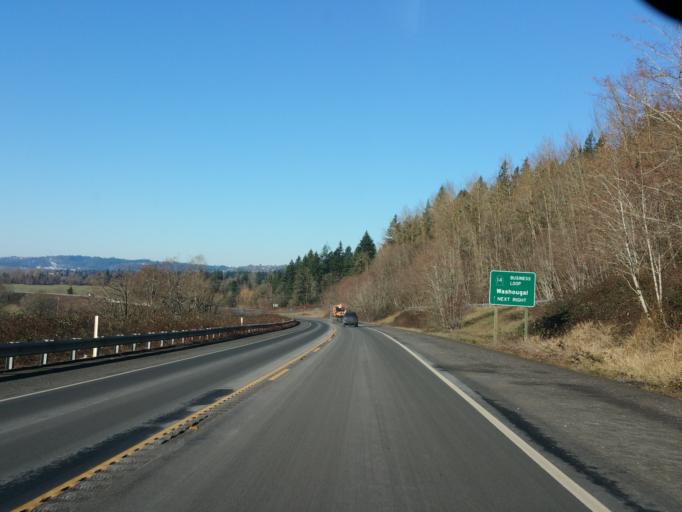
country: US
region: Washington
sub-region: Clark County
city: Washougal
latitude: 45.5702
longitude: -122.2945
